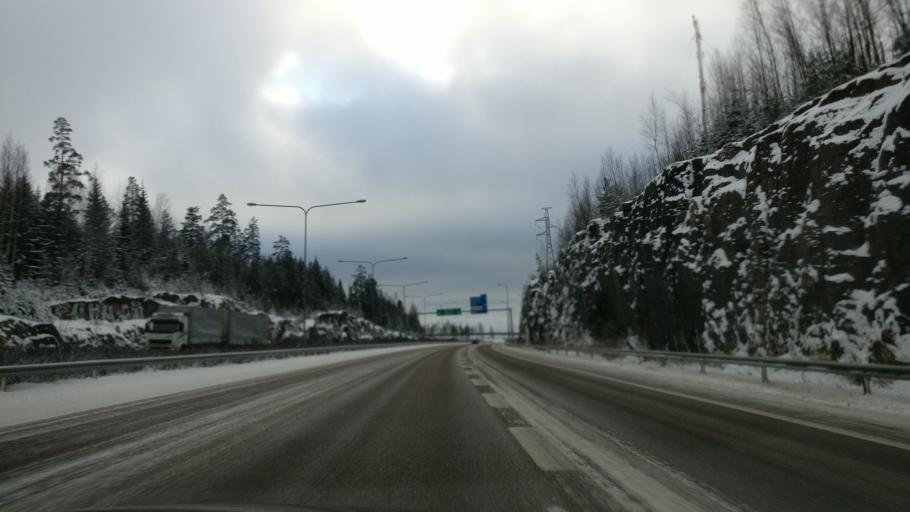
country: FI
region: Paijanne Tavastia
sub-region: Lahti
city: Lahti
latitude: 60.9757
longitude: 25.7282
